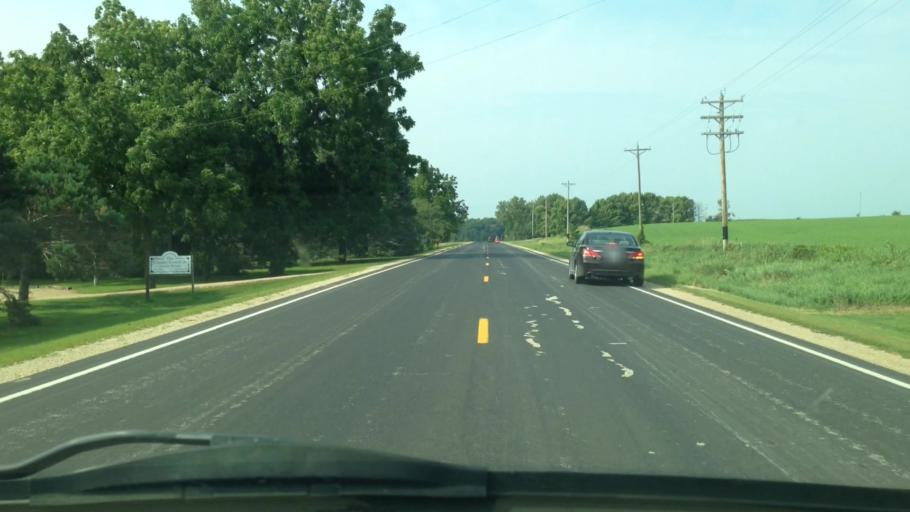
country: US
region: Minnesota
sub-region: Winona County
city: Lewiston
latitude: 43.9598
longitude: -91.9543
